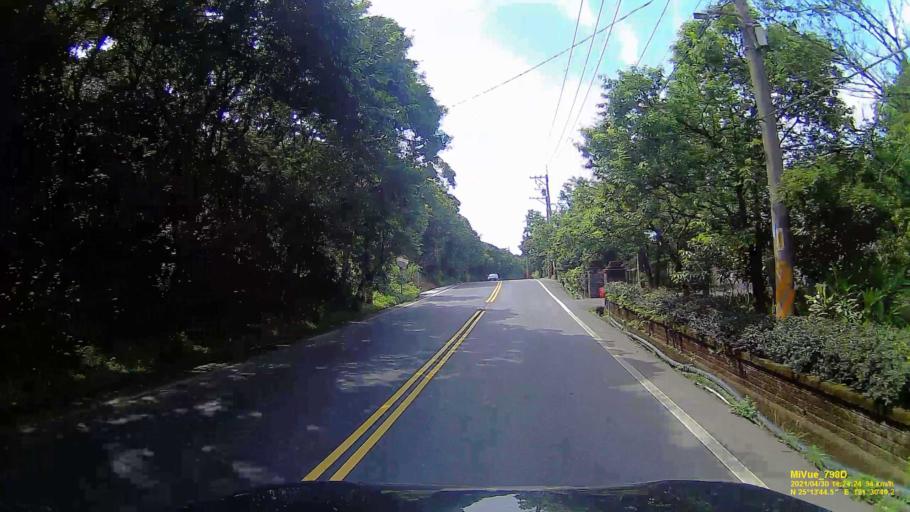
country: TW
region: Taipei
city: Taipei
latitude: 25.2292
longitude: 121.5134
